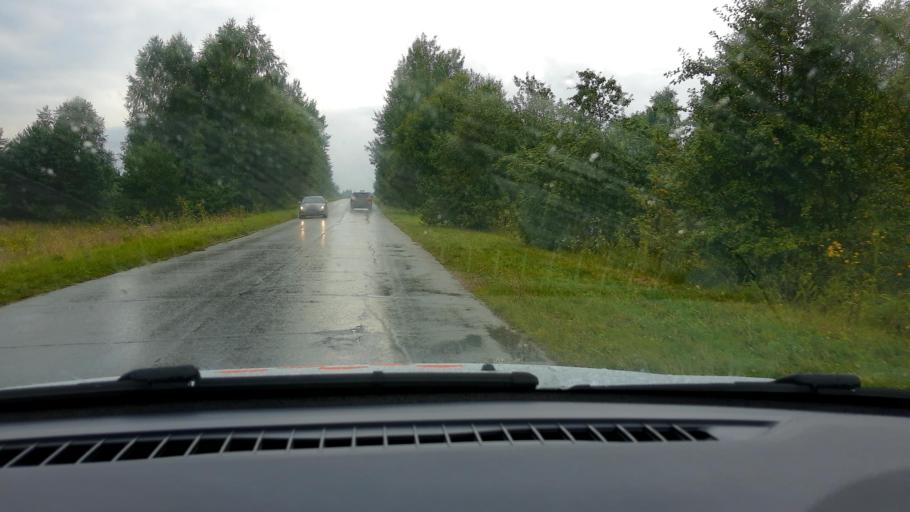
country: RU
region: Nizjnij Novgorod
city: Surovatikha
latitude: 55.9456
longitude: 43.9197
